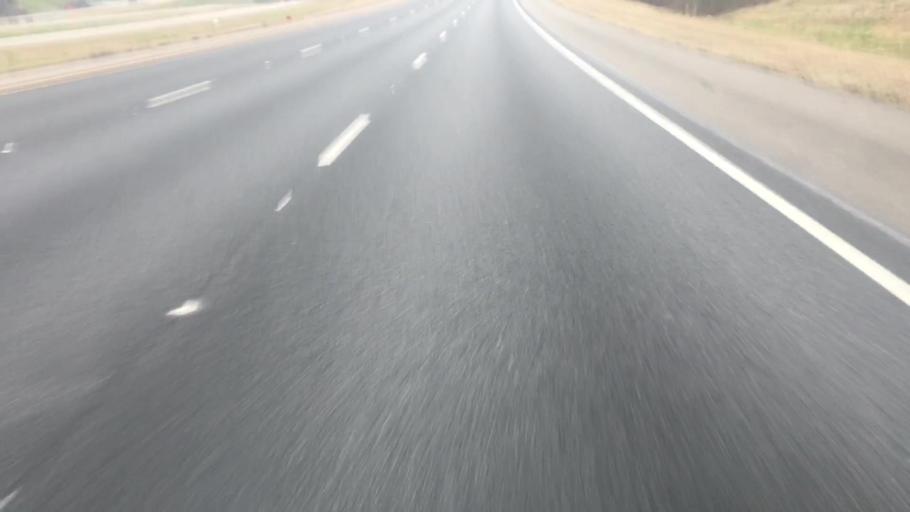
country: US
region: Alabama
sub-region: Jefferson County
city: Fultondale
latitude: 33.5779
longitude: -86.8229
